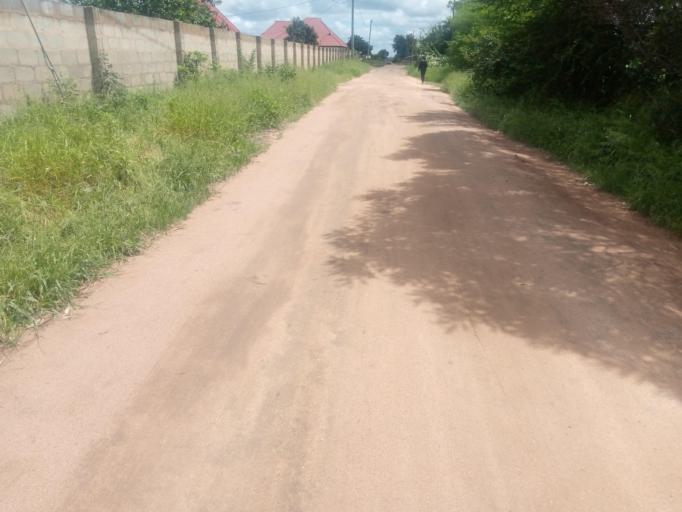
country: TZ
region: Dodoma
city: Dodoma
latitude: -6.1219
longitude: 35.7397
